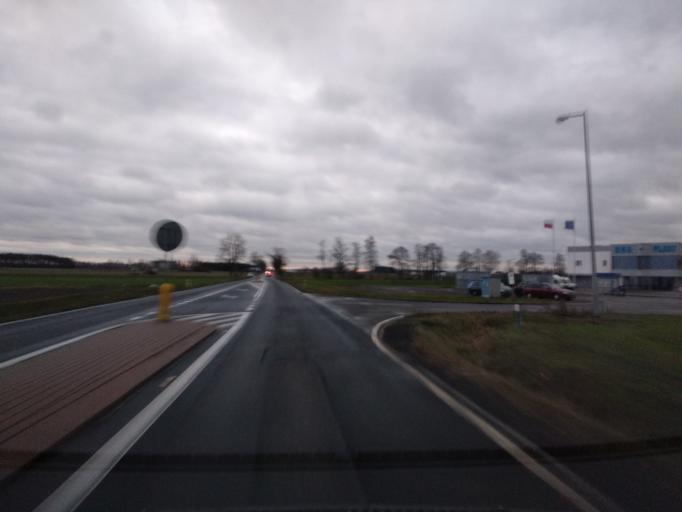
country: PL
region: Greater Poland Voivodeship
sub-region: Powiat koninski
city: Stare Miasto
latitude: 52.1476
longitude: 18.1994
